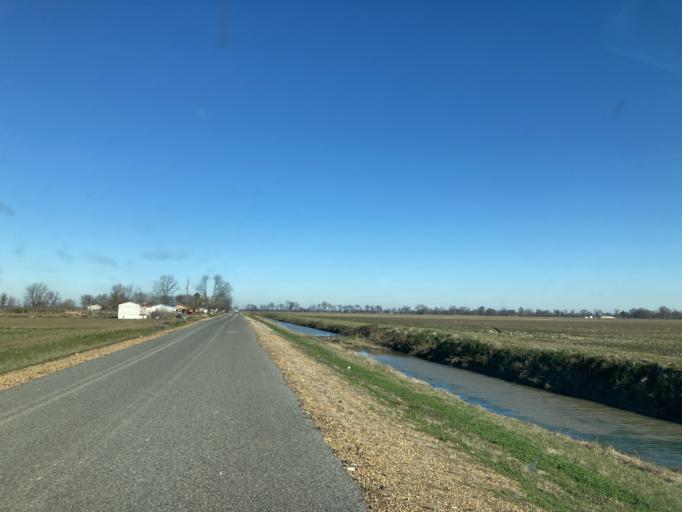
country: US
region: Mississippi
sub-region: Yazoo County
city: Yazoo City
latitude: 32.9531
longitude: -90.6055
